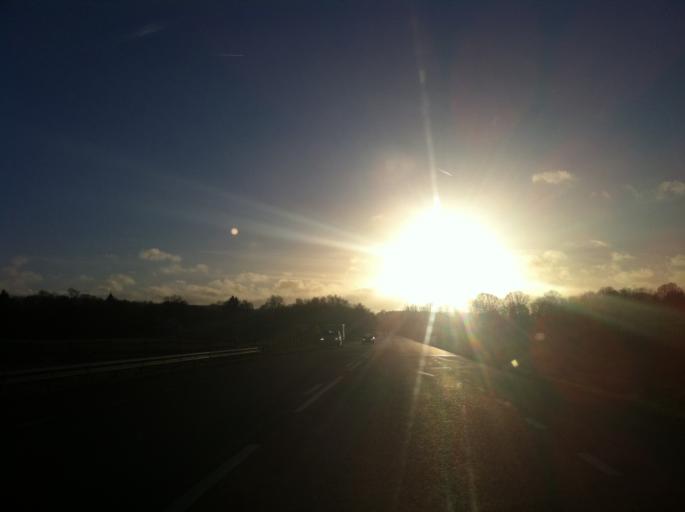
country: SE
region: Skane
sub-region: Hassleholms Kommun
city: Tormestorp
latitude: 56.1030
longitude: 13.7795
